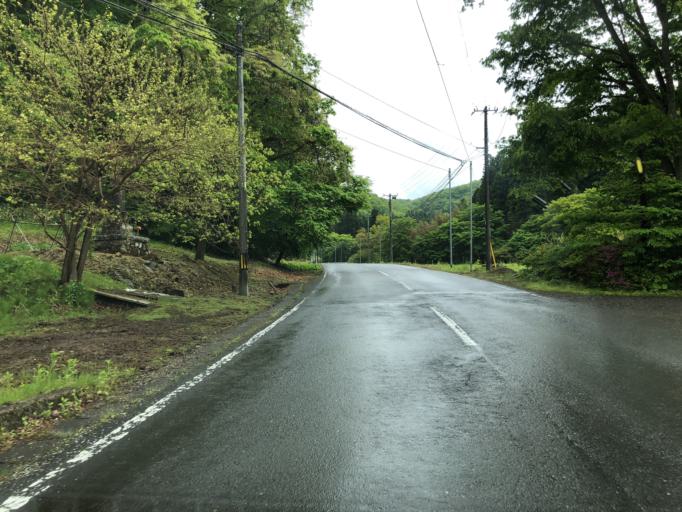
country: JP
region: Fukushima
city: Ishikawa
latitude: 36.9892
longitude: 140.6173
